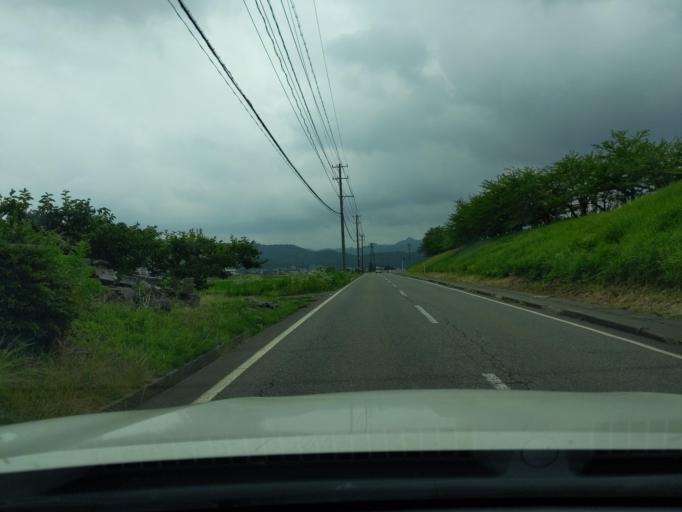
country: JP
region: Niigata
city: Kashiwazaki
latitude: 37.3476
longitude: 138.6011
